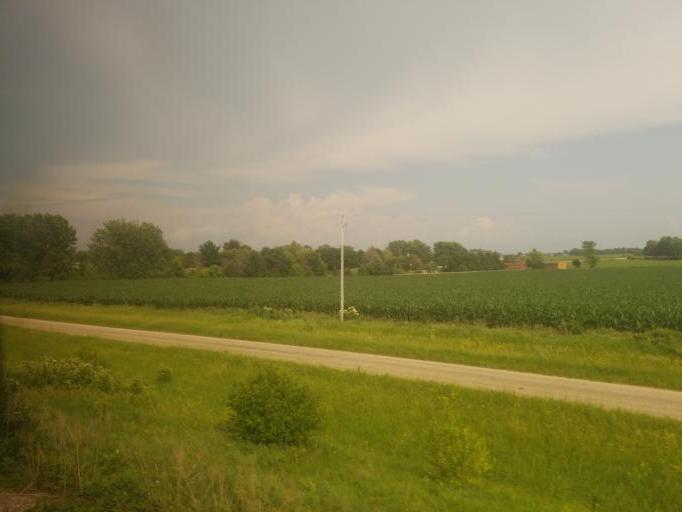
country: US
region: Illinois
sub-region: Bureau County
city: Princeton
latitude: 41.3193
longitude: -89.6877
